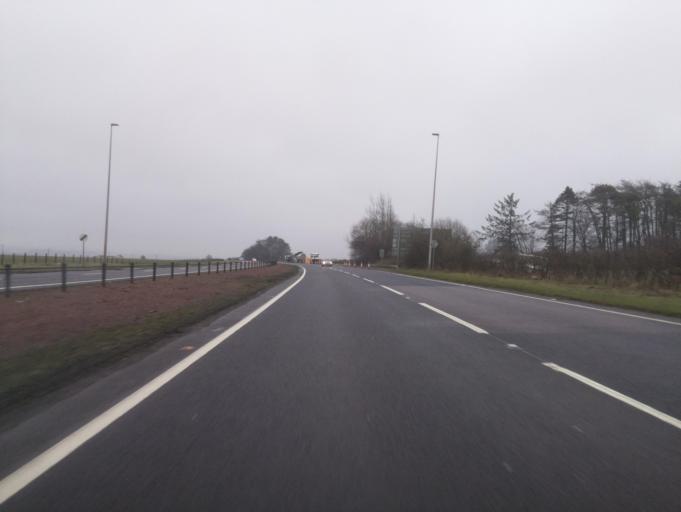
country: GB
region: Scotland
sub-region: Clackmannanshire
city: Menstrie
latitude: 56.2427
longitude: -3.8728
